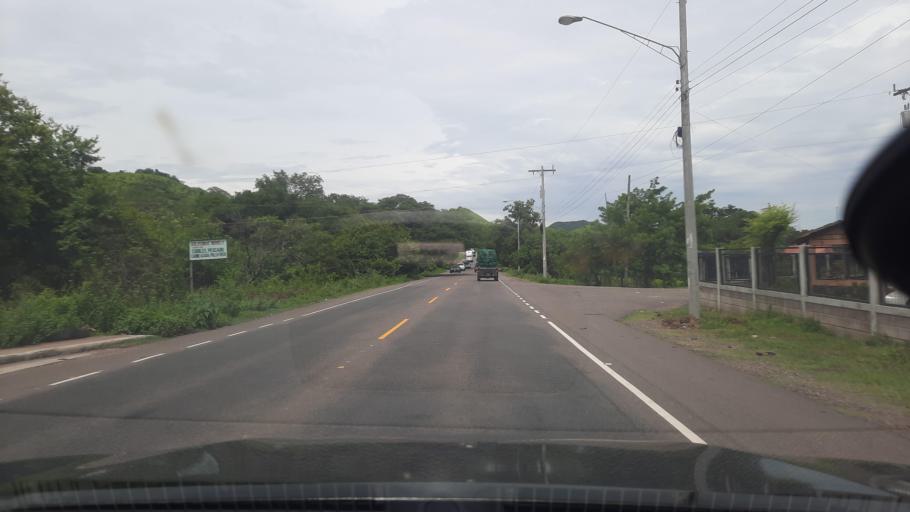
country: HN
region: Valle
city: Goascoran
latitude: 13.5500
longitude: -87.6447
